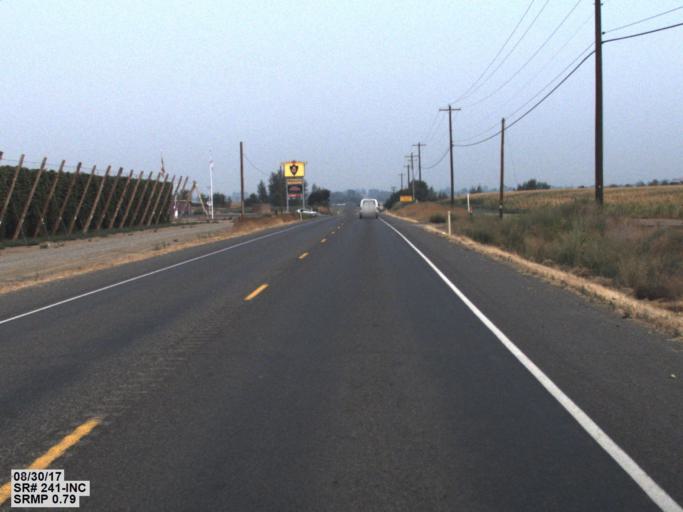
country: US
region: Washington
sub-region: Yakima County
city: Mabton
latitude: 46.2228
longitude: -119.9996
